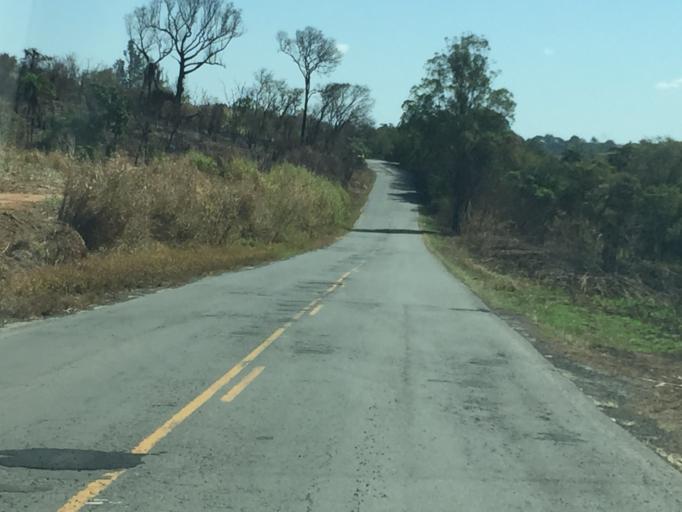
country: BR
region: Sao Paulo
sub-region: Moji-Guacu
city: Mogi-Gaucu
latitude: -22.3569
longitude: -46.8691
